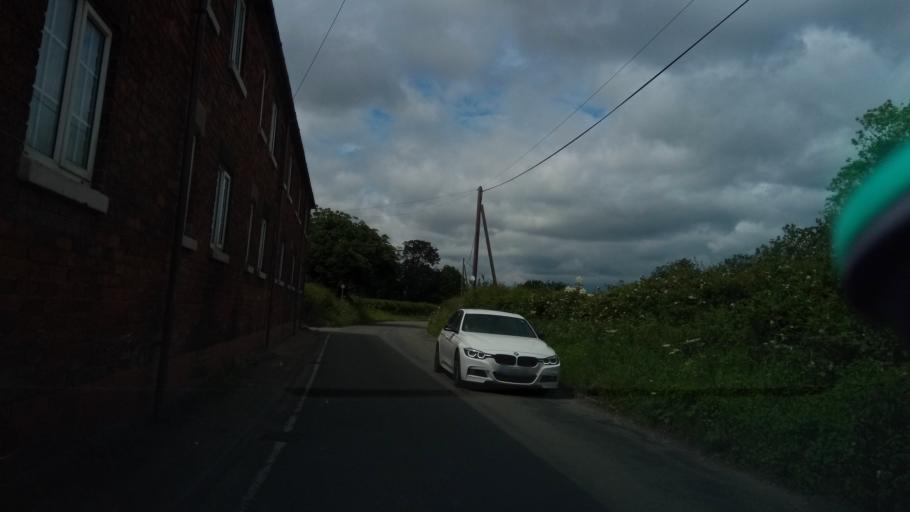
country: GB
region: England
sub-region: Derbyshire
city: Findern
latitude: 52.8661
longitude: -1.5214
